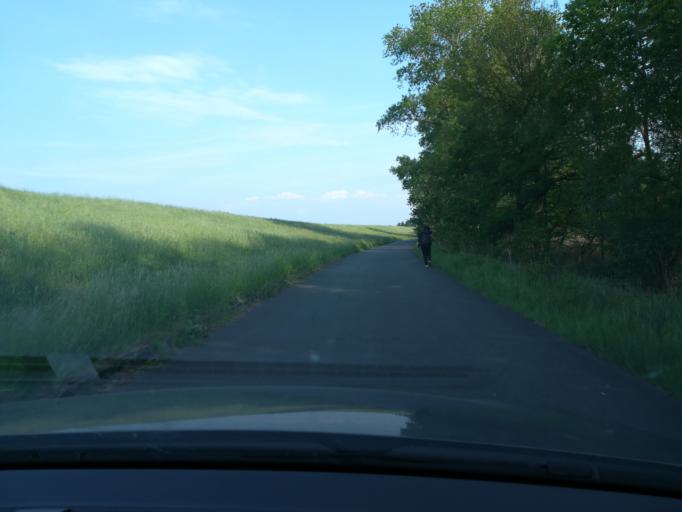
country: DE
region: Lower Saxony
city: Artlenburg
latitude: 53.3822
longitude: 10.4689
